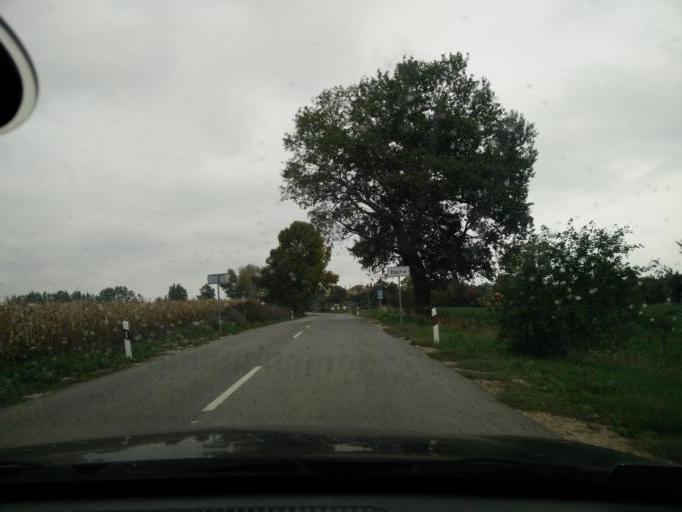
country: HU
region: Komarom-Esztergom
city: Bajna
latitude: 47.6576
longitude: 18.5864
